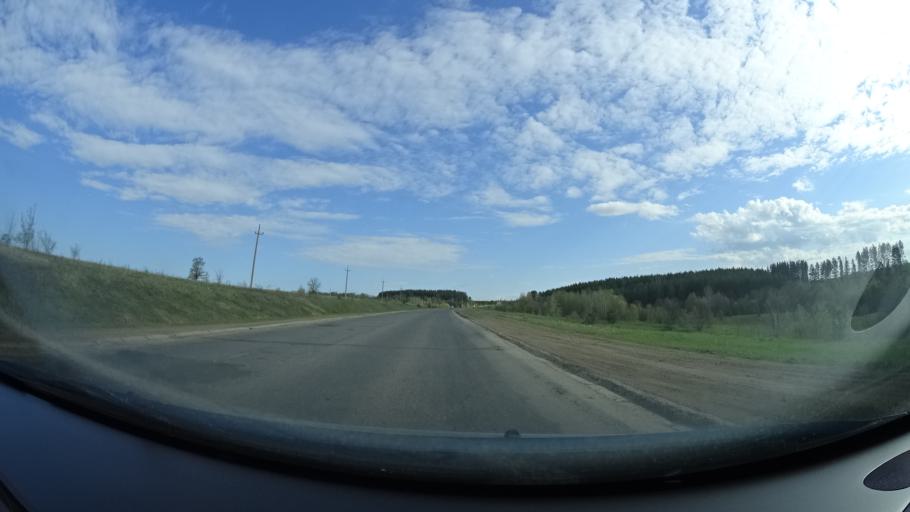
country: RU
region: Bashkortostan
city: Blagoveshchensk
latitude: 55.0809
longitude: 55.8072
